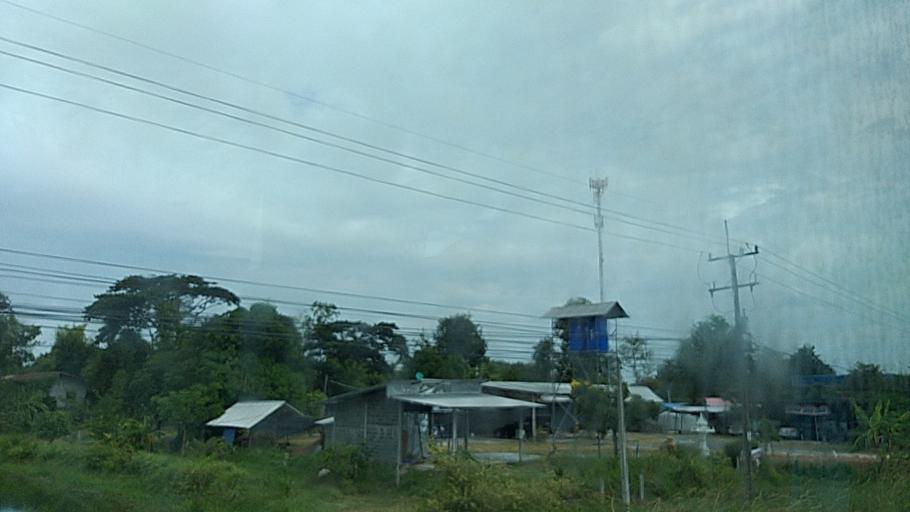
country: TH
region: Roi Et
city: Changhan
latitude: 16.0967
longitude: 103.5358
